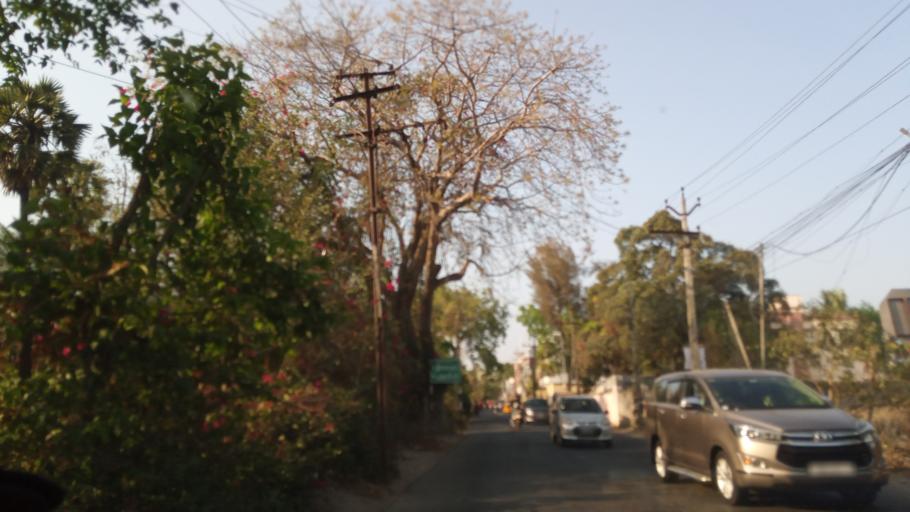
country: IN
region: Tamil Nadu
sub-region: Kancheepuram
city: Manappakkam
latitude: 13.0218
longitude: 80.1834
